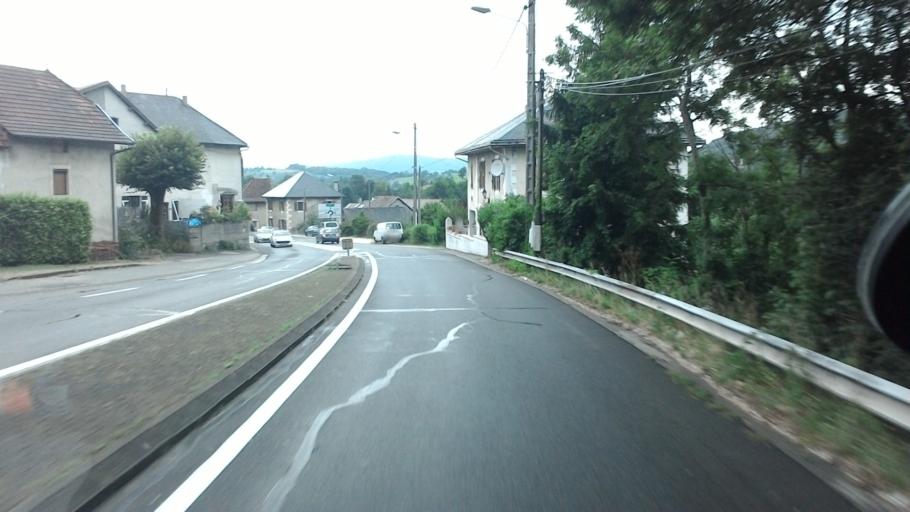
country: FR
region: Rhone-Alpes
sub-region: Departement de la Savoie
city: Le Bourget-du-Lac
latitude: 45.6903
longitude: 5.8199
